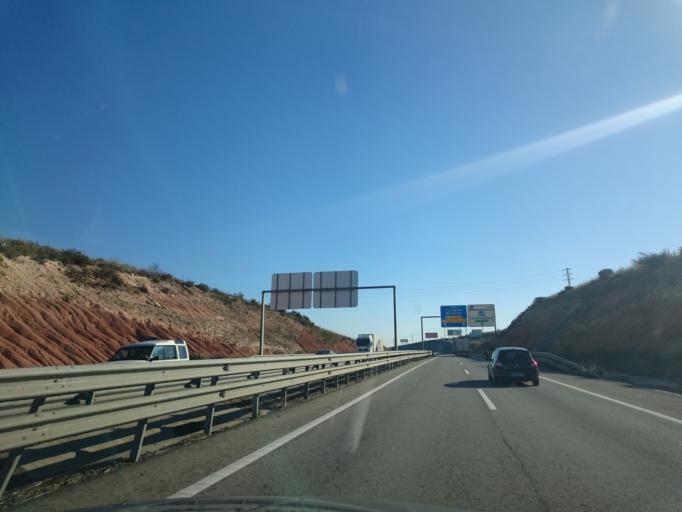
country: ES
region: Catalonia
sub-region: Provincia de Tarragona
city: Constanti
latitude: 41.1261
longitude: 1.1893
